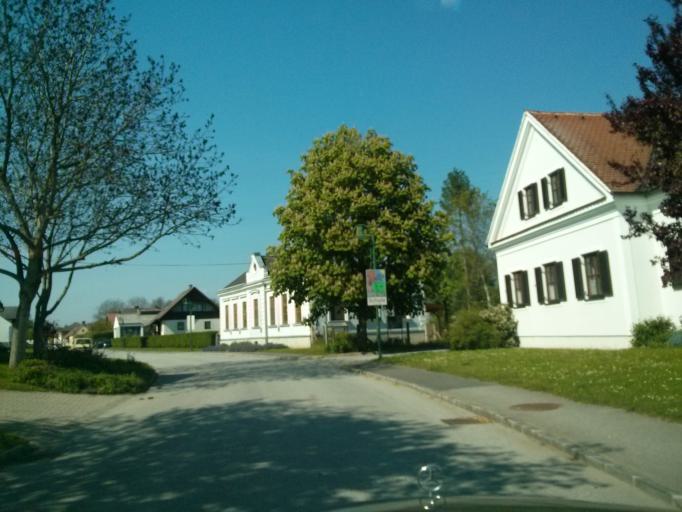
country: AT
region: Burgenland
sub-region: Politischer Bezirk Oberwart
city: Bad Tatzmannsdorf
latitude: 47.3169
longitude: 16.2049
